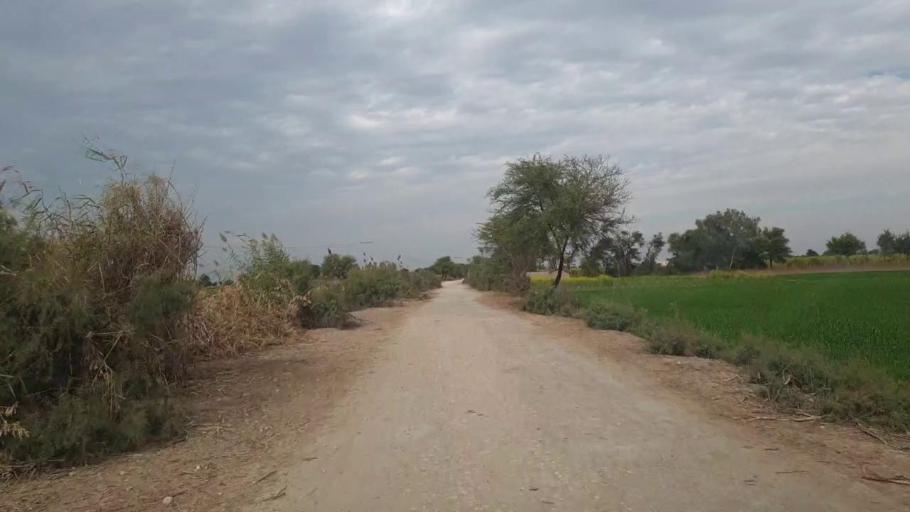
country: PK
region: Sindh
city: Jhol
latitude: 26.0174
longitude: 68.8755
